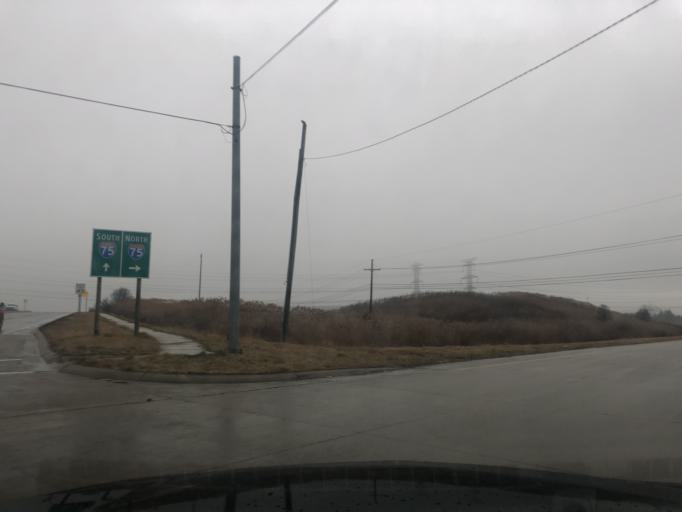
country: US
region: Michigan
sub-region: Wayne County
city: Rockwood
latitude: 42.0955
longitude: -83.2390
